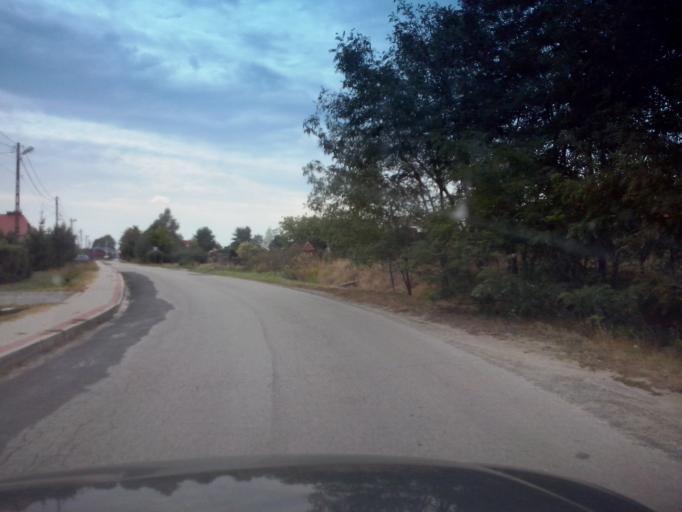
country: PL
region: Subcarpathian Voivodeship
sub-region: Powiat stalowowolski
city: Stalowa Wola
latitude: 50.6128
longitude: 22.0138
